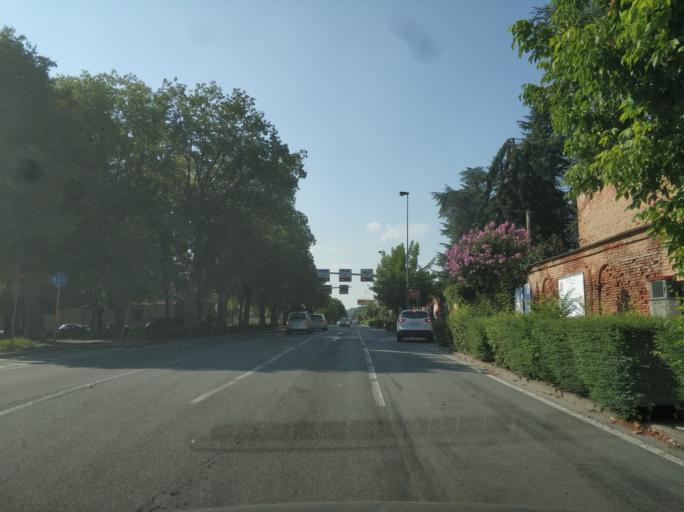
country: IT
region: Piedmont
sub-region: Provincia di Cuneo
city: Bra
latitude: 44.7020
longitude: 7.8475
